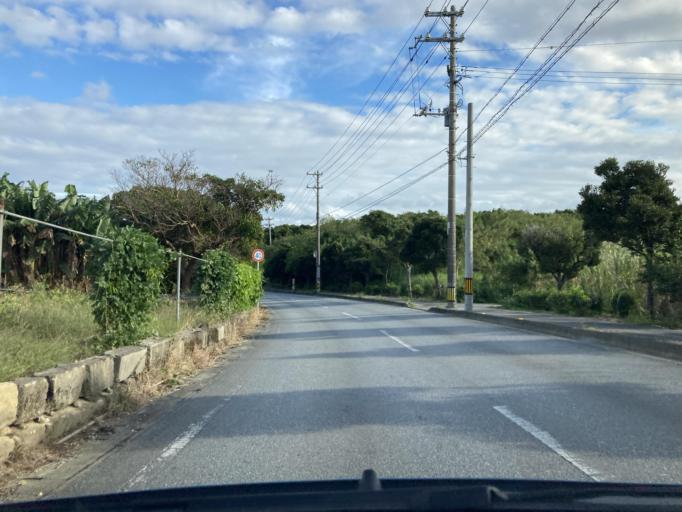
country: JP
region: Okinawa
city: Itoman
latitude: 26.1344
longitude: 127.7502
